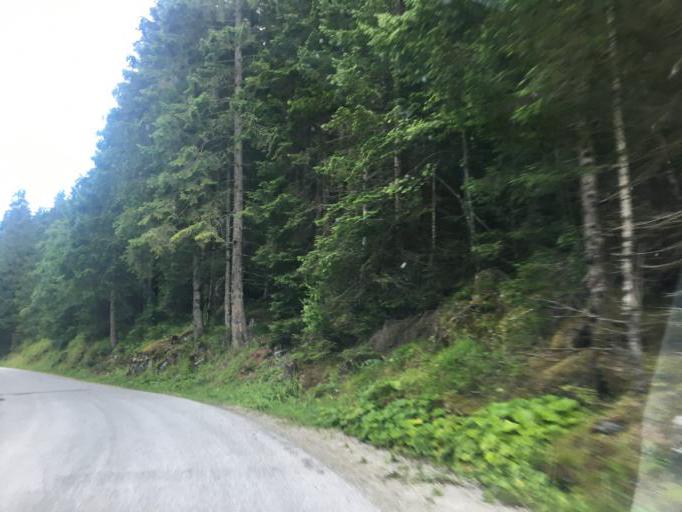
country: AT
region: Styria
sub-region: Politischer Bezirk Liezen
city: Haus
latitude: 47.3392
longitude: 13.7418
